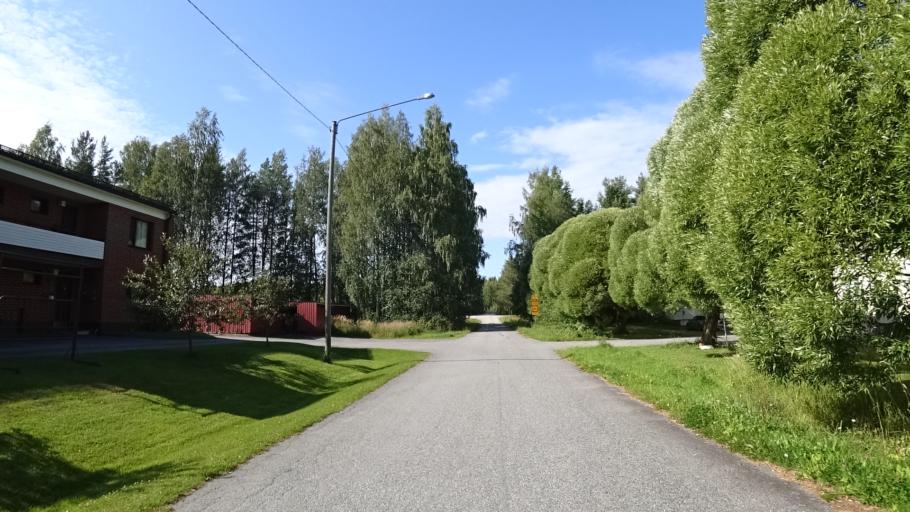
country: FI
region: North Karelia
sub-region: Joensuu
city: Eno
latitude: 62.8001
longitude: 30.1494
